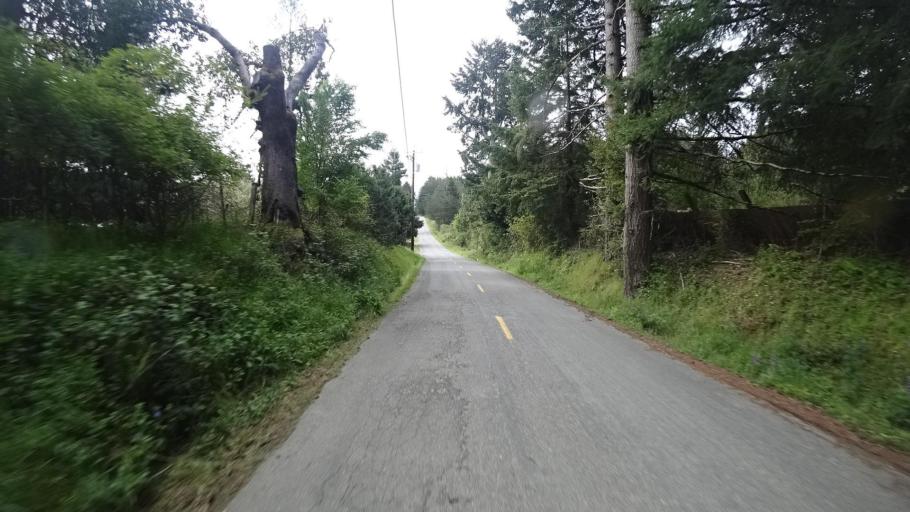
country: US
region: California
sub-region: Humboldt County
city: Redway
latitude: 40.2992
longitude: -123.8216
